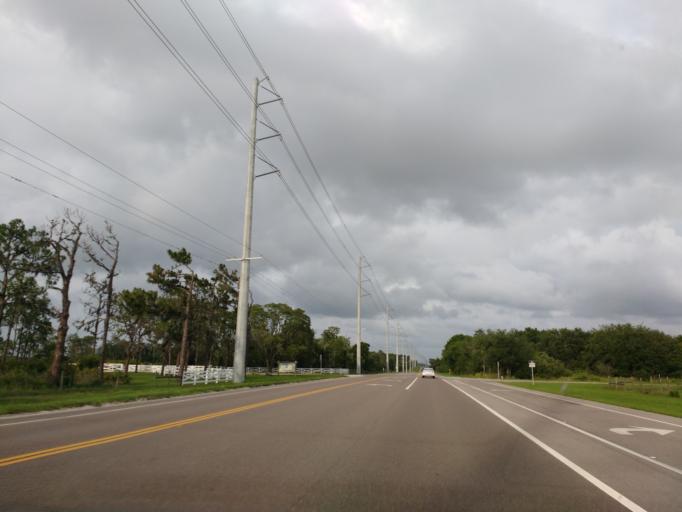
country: US
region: Florida
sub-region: Sarasota County
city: The Meadows
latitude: 27.4752
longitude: -82.3475
